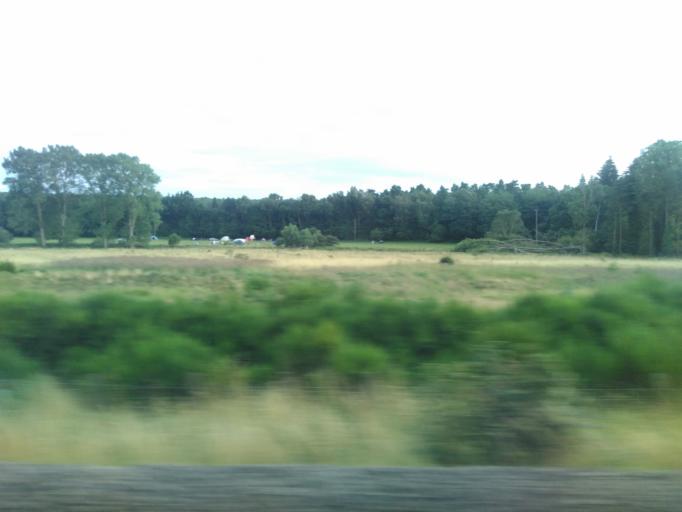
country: GB
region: England
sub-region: Norfolk
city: Thetford
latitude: 52.4528
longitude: 0.6936
